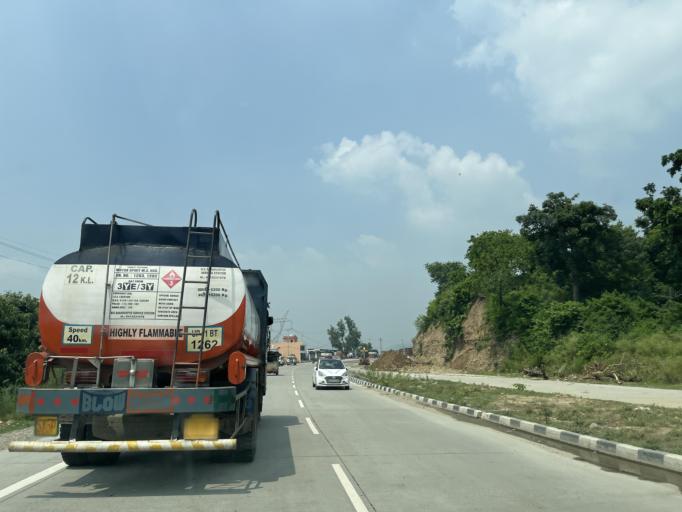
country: IN
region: Uttarakhand
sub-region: Haridwar
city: Haridwar
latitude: 29.8477
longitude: 78.1855
